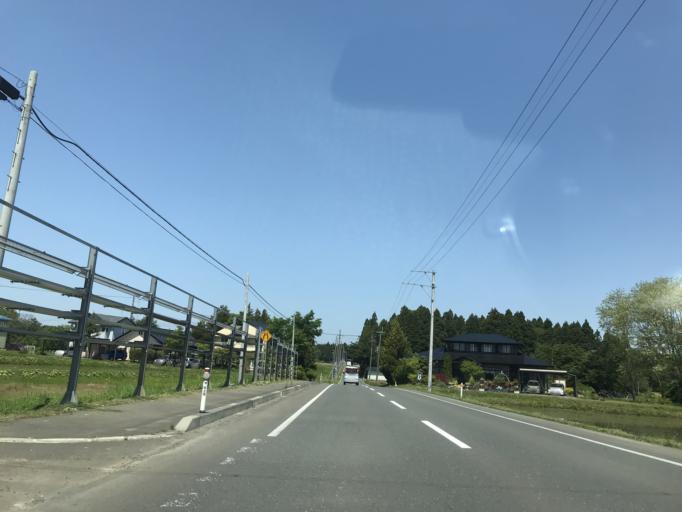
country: JP
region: Iwate
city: Kitakami
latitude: 39.2624
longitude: 141.0629
